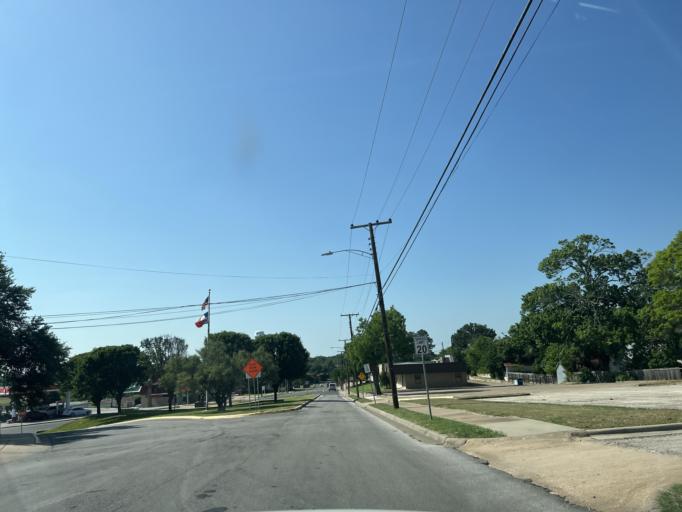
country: US
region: Texas
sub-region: Washington County
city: Brenham
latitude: 30.1688
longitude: -96.3985
